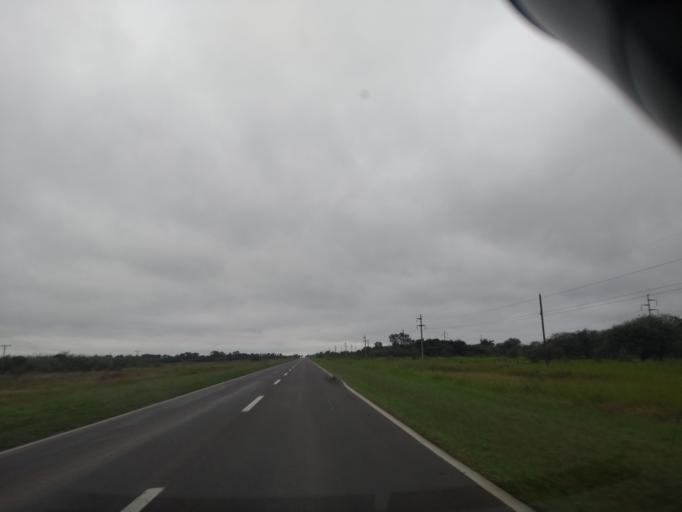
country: AR
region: Chaco
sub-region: Departamento de Quitilipi
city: Quitilipi
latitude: -26.8649
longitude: -60.2705
